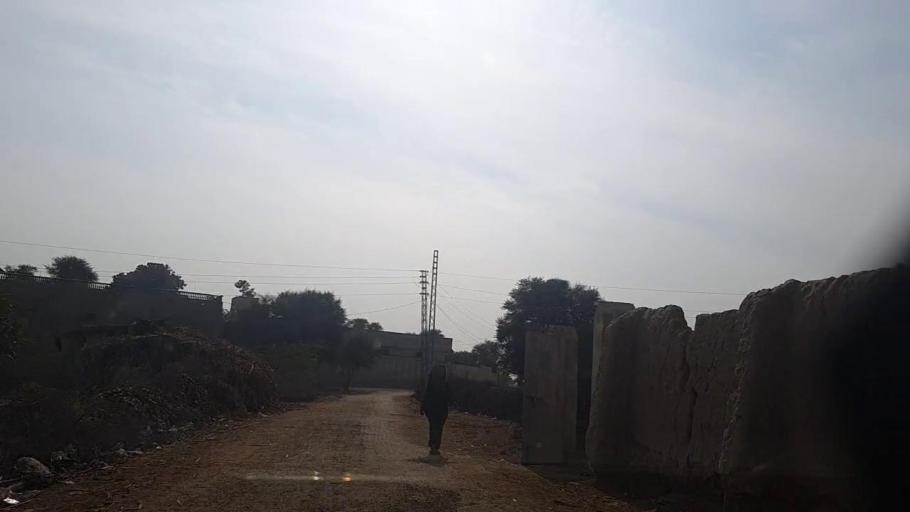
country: PK
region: Sindh
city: Daur
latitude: 26.4023
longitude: 68.2386
